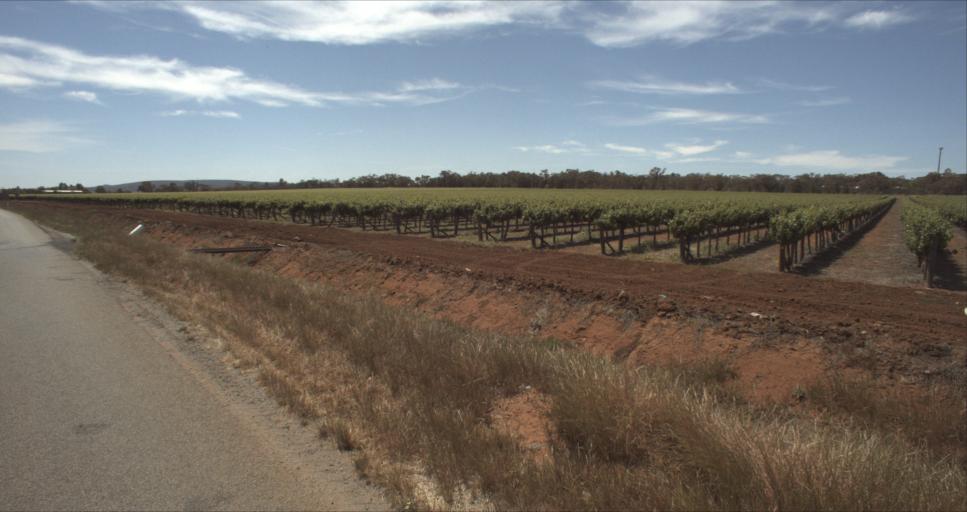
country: AU
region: New South Wales
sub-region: Leeton
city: Leeton
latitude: -34.5647
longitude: 146.4519
